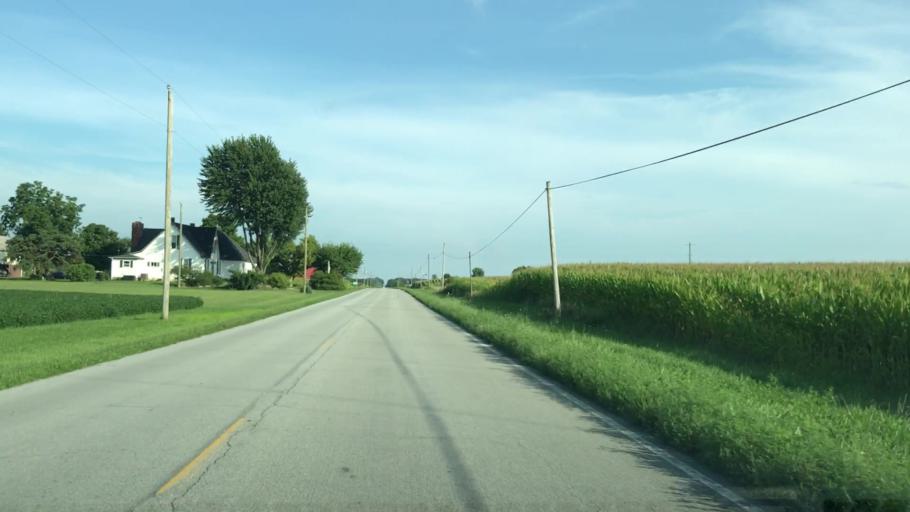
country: US
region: Ohio
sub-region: Union County
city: Marysville
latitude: 40.2059
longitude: -83.3511
